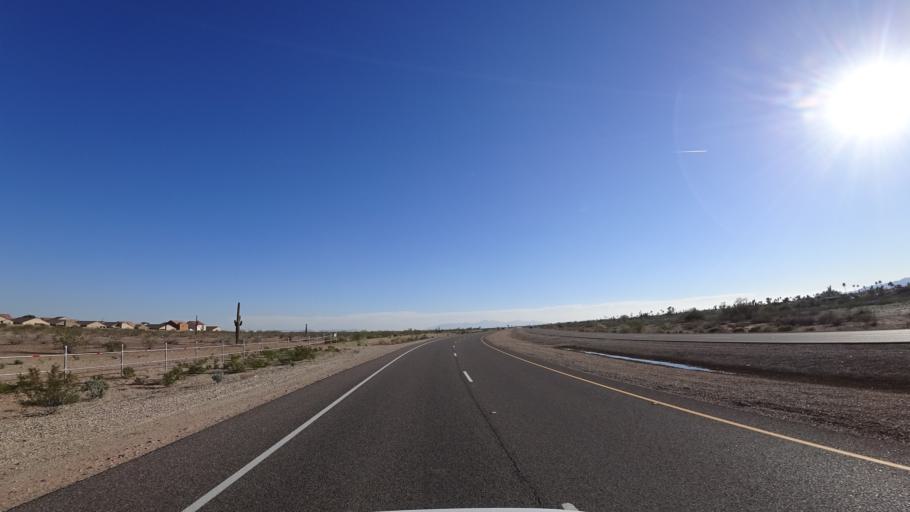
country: US
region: Arizona
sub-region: Maricopa County
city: Sun City West
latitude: 33.6804
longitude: -112.3230
